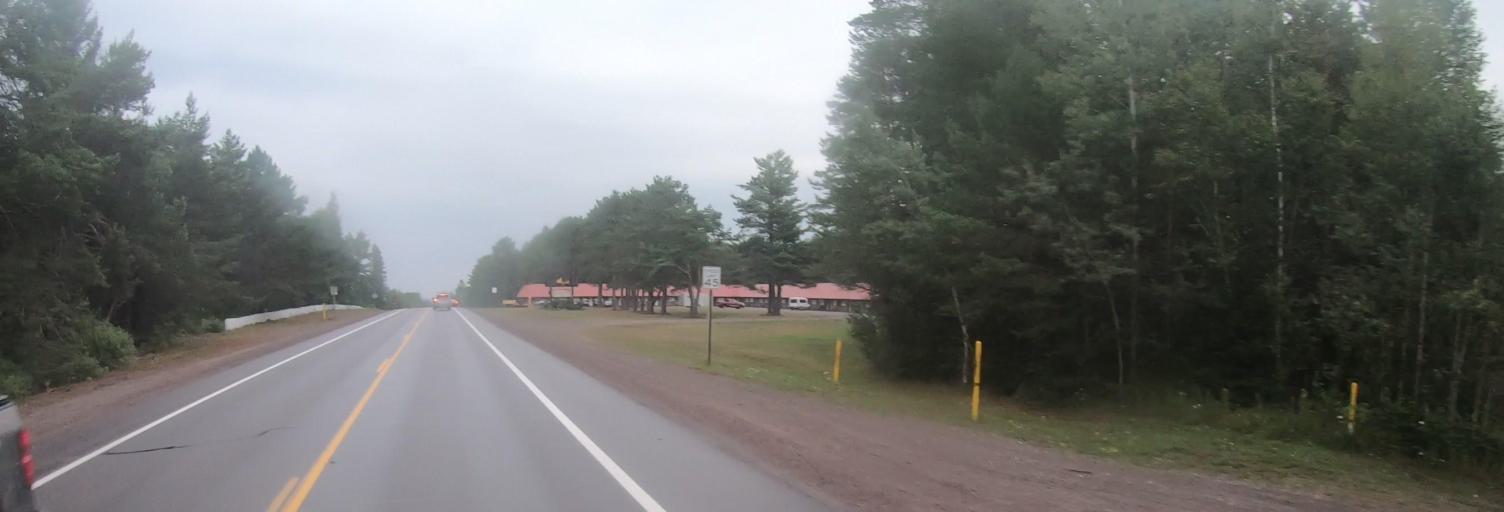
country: US
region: Michigan
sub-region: Houghton County
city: Laurium
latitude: 47.2545
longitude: -88.4329
